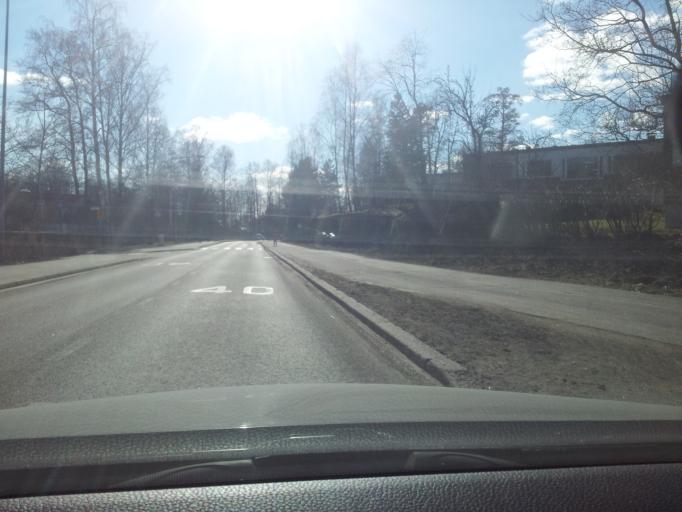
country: FI
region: Uusimaa
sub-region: Helsinki
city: Koukkuniemi
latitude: 60.1598
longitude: 24.7738
